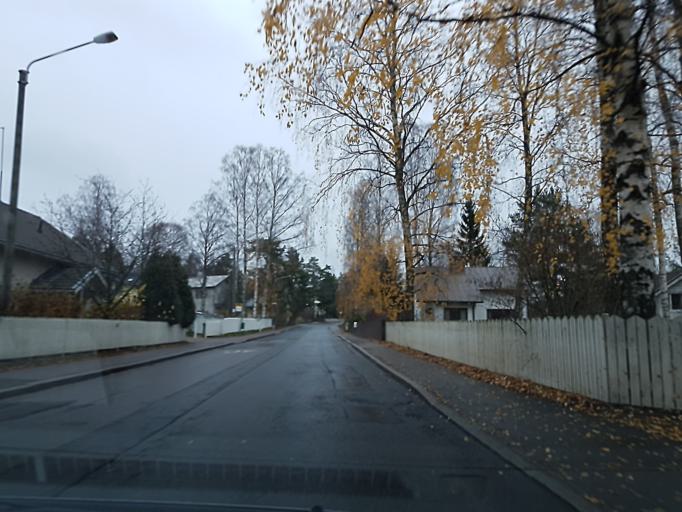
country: FI
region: Uusimaa
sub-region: Helsinki
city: Vantaa
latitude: 60.2264
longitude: 25.0832
